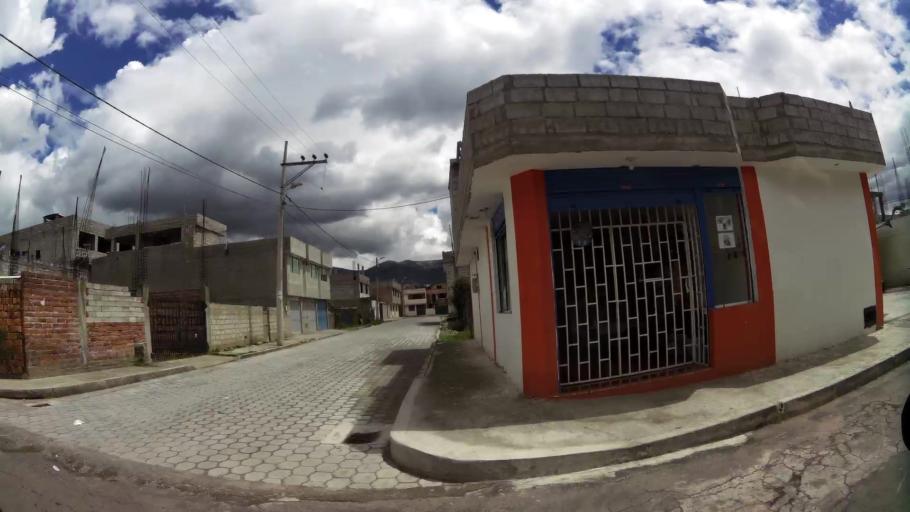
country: EC
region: Pichincha
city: Sangolqui
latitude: -0.3332
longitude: -78.5358
